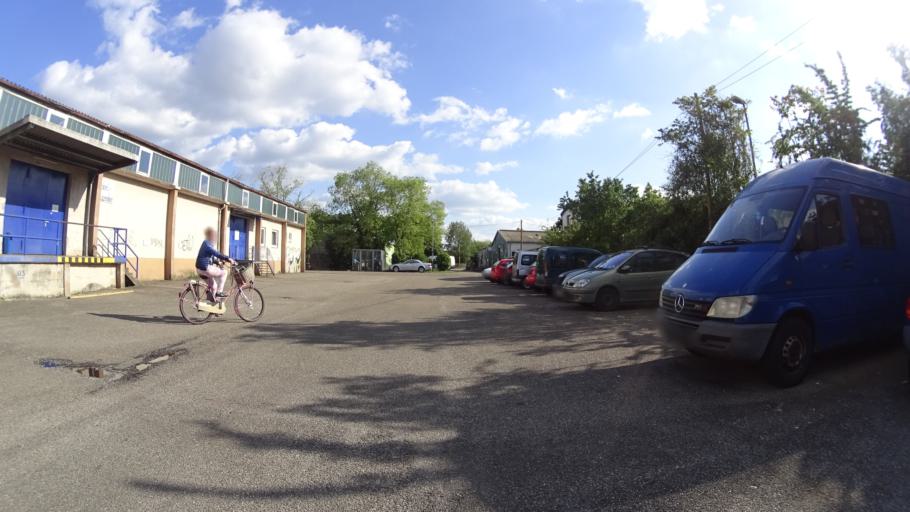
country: DE
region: Baden-Wuerttemberg
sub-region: Karlsruhe Region
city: Karlsruhe
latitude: 49.0291
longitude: 8.3839
